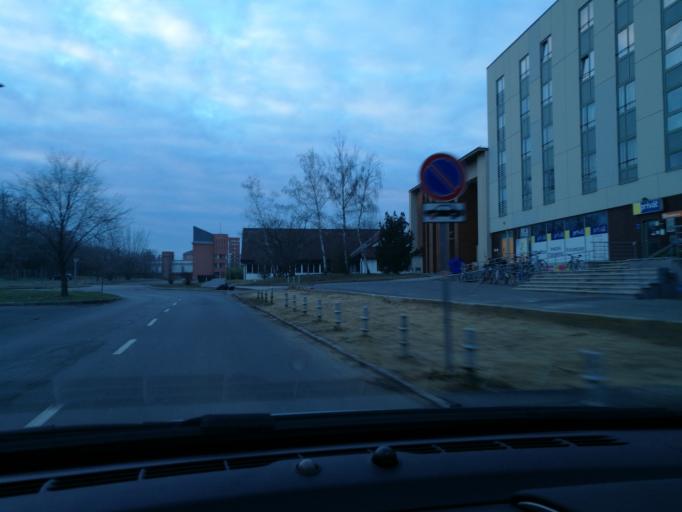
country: HU
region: Szabolcs-Szatmar-Bereg
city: Nyiregyhaza
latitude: 47.9719
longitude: 21.7125
